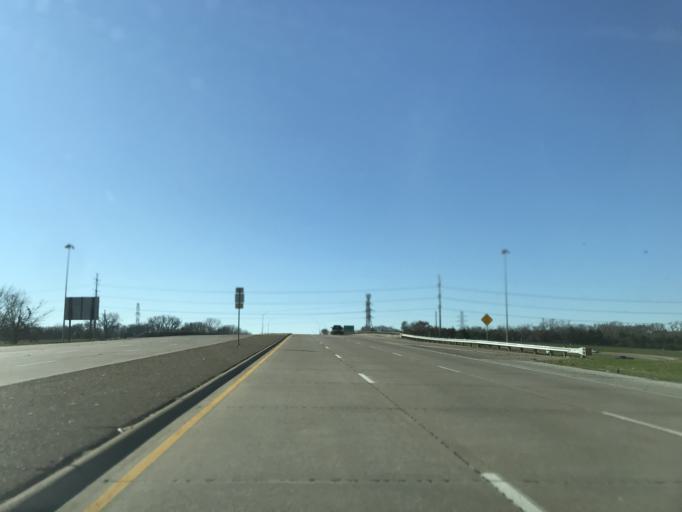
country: US
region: Texas
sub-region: Dallas County
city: Hutchins
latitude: 32.7017
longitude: -96.7516
